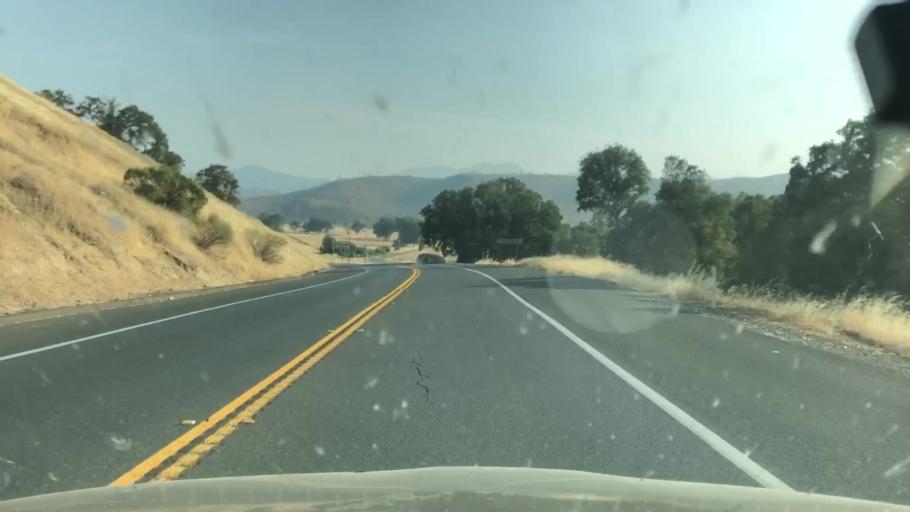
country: US
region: California
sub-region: Lake County
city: Hidden Valley Lake
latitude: 38.8123
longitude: -122.5728
